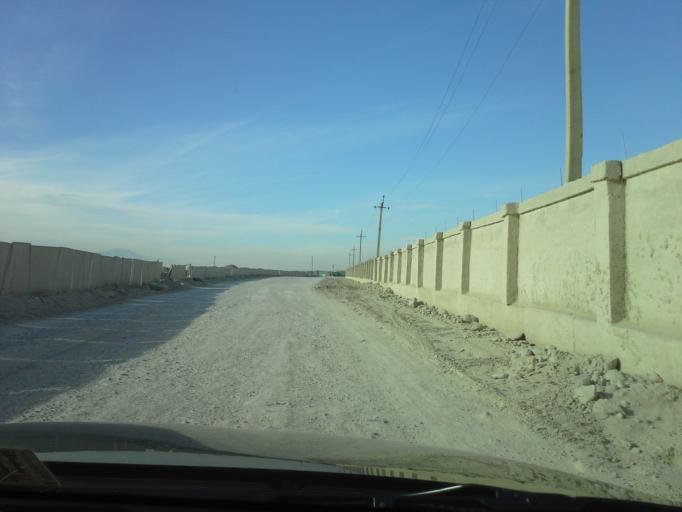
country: TM
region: Ahal
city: Abadan
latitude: 38.0300
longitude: 58.1614
